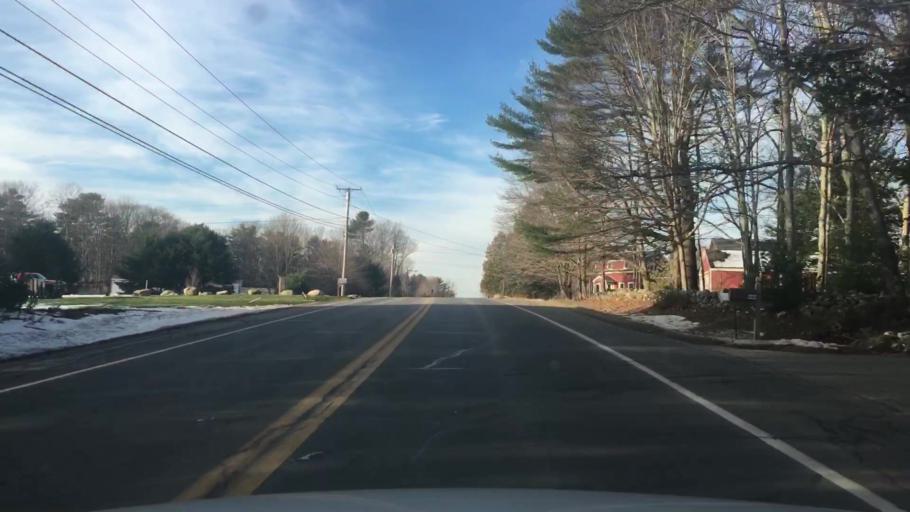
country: US
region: Maine
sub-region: Lincoln County
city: Wiscasset
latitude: 44.0475
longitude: -69.6790
